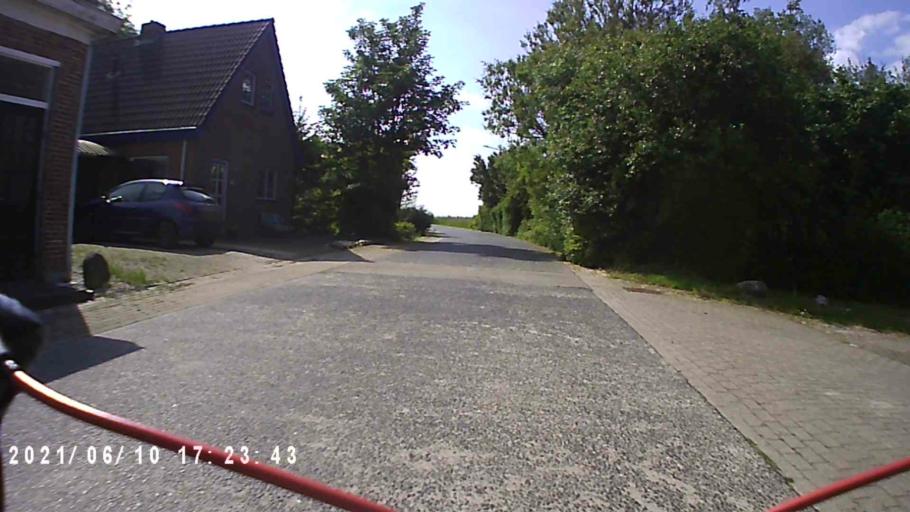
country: NL
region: Friesland
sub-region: Gemeente Kollumerland en Nieuwkruisland
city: Kollum
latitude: 53.2970
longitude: 6.2282
